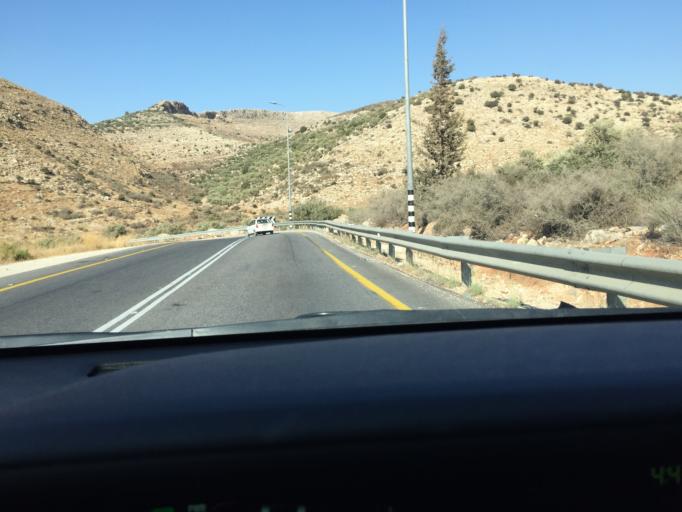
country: PS
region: West Bank
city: Al Lubban al Gharbi
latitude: 32.0484
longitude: 35.0481
